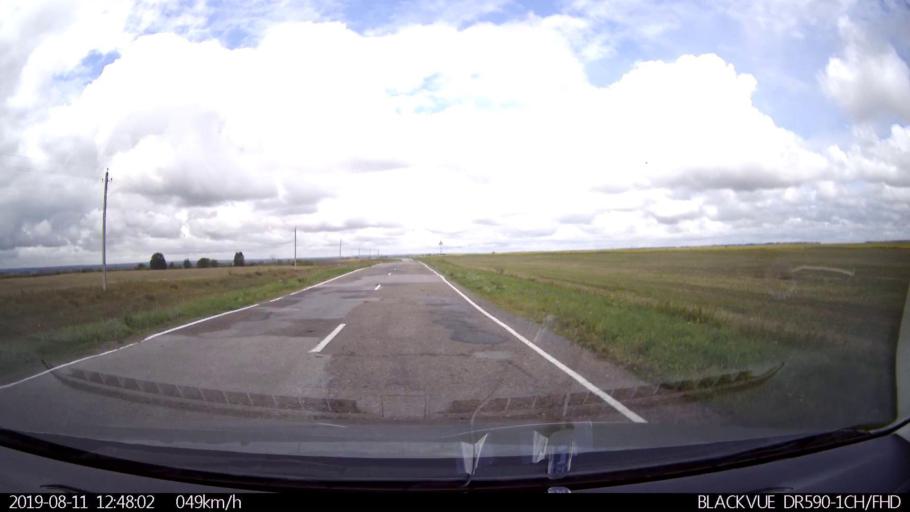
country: RU
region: Ulyanovsk
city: Ignatovka
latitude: 53.8721
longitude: 47.7028
